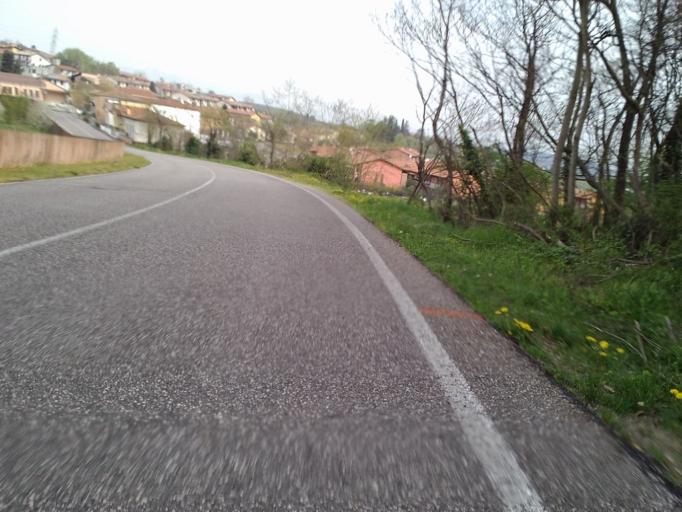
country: IT
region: Veneto
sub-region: Provincia di Verona
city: Rosegaferro
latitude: 45.3750
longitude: 10.7973
